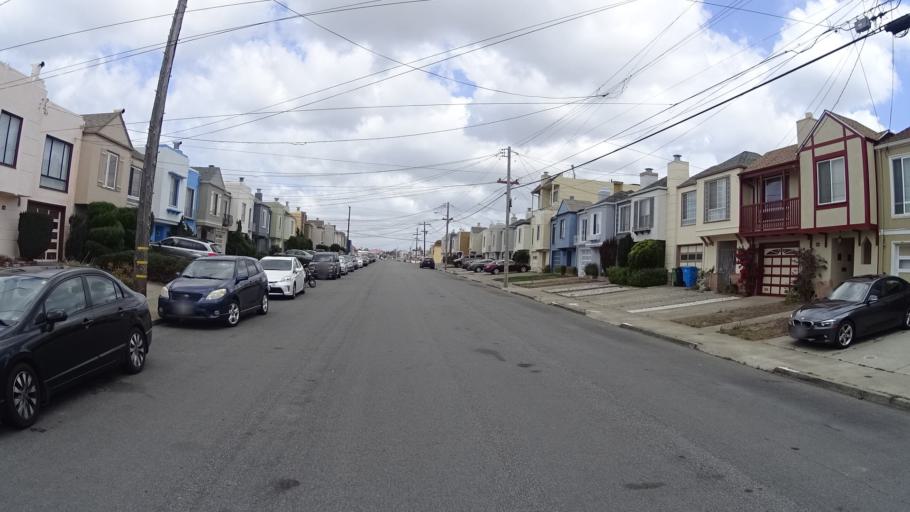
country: US
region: California
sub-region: San Mateo County
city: Daly City
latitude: 37.7353
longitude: -122.4956
